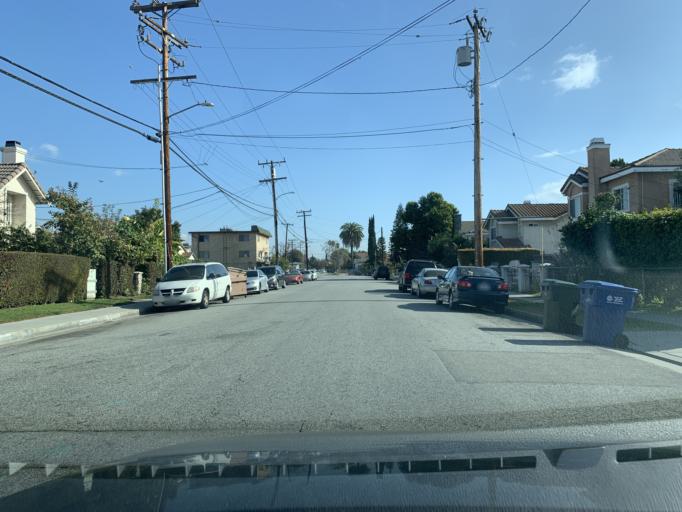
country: US
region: California
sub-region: Los Angeles County
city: South El Monte
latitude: 34.0644
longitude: -118.0603
